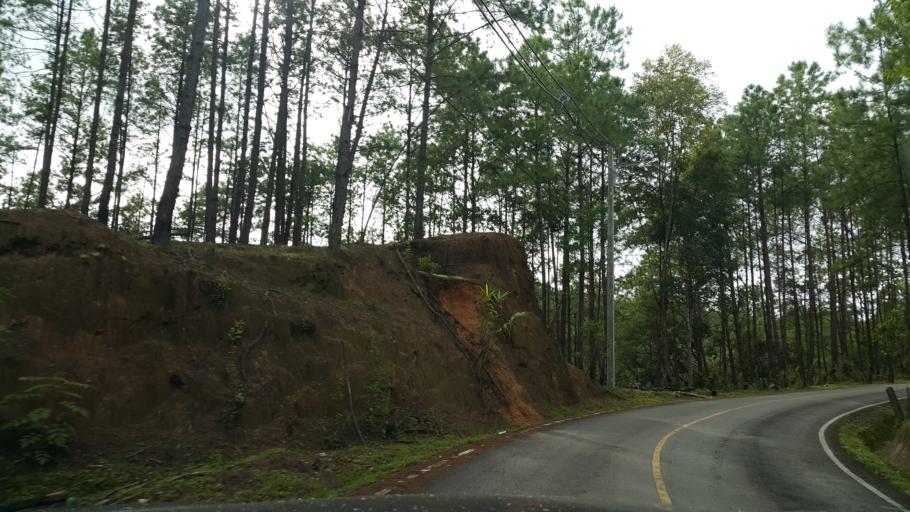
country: TH
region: Chiang Mai
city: Samoeng
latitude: 18.9093
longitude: 98.5050
